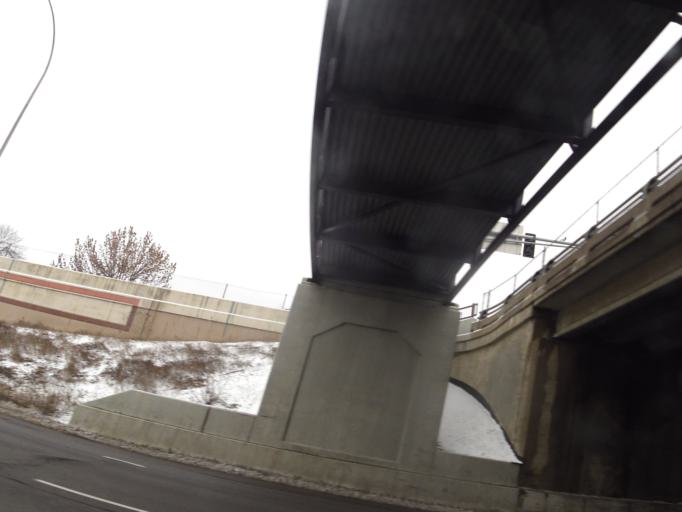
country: US
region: Minnesota
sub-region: Hennepin County
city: Richfield
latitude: 44.8623
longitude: -93.2581
